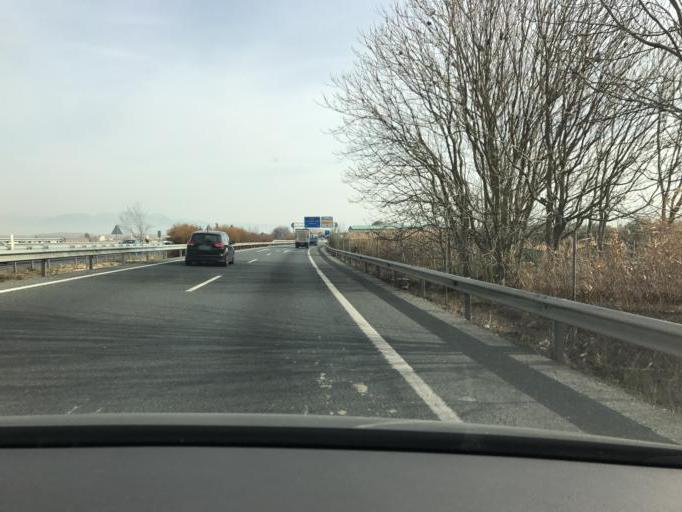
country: ES
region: Andalusia
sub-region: Provincia de Granada
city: Chauchina
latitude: 37.1918
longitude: -3.7565
